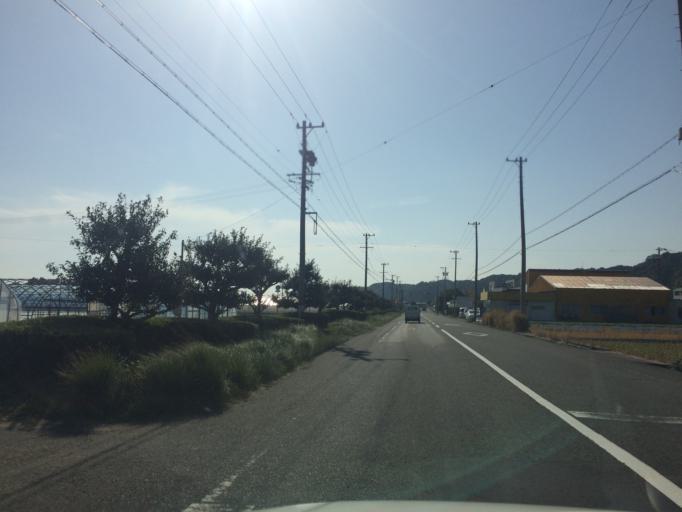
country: JP
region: Shizuoka
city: Sagara
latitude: 34.7196
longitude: 138.2181
